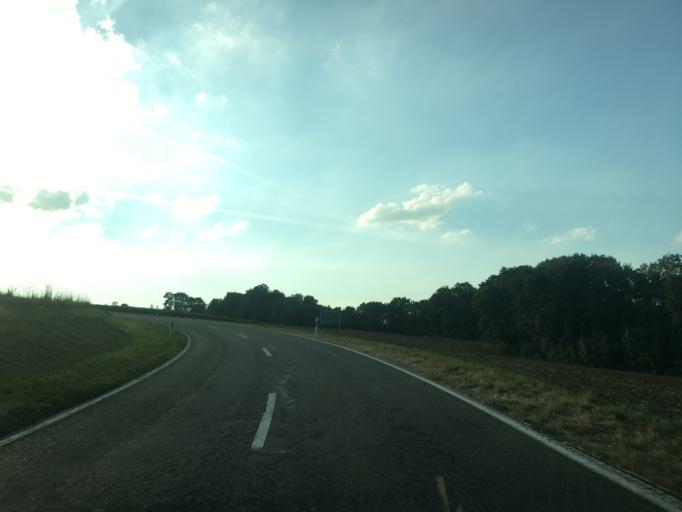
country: DE
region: Baden-Wuerttemberg
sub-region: Tuebingen Region
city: Obermarchtal
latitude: 48.2366
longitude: 9.5649
